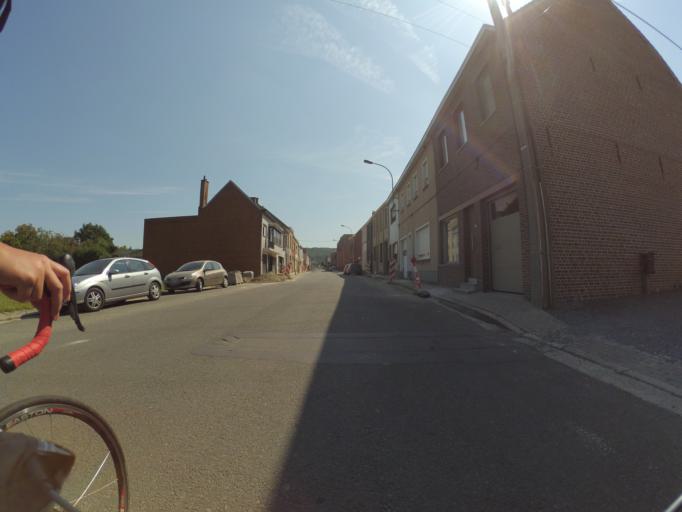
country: BE
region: Flanders
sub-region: Provincie West-Vlaanderen
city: Avelgem
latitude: 50.7722
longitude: 3.4807
